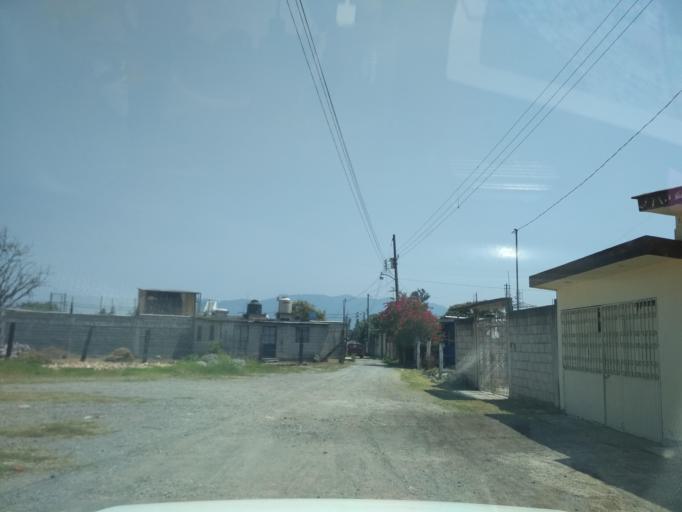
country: MX
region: Veracruz
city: Rio Blanco
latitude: 18.8368
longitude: -97.1117
